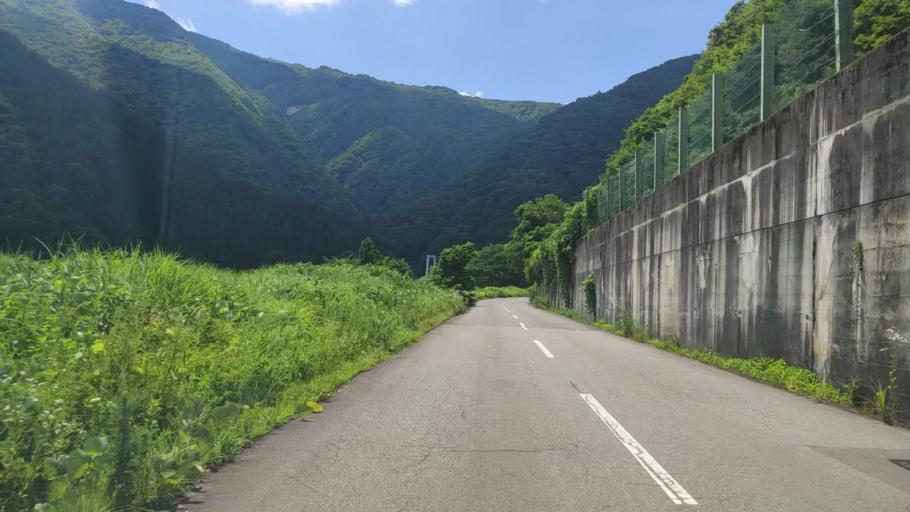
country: JP
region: Fukui
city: Ono
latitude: 35.8991
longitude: 136.5268
